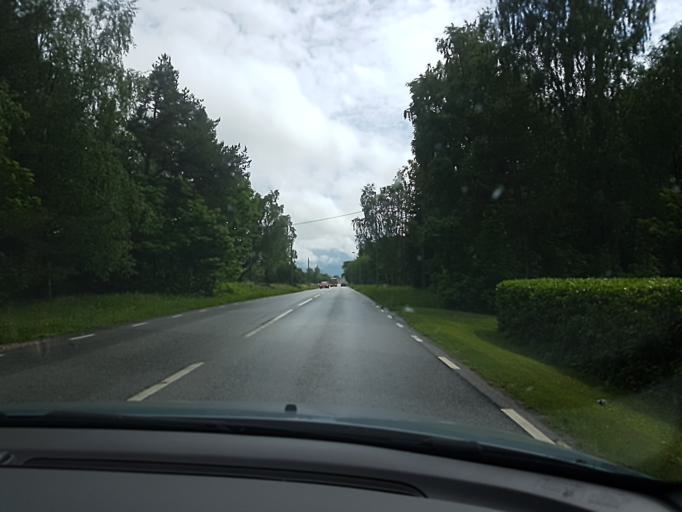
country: SE
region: Uppsala
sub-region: Osthammars Kommun
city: OEsthammar
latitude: 60.2946
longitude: 18.2844
